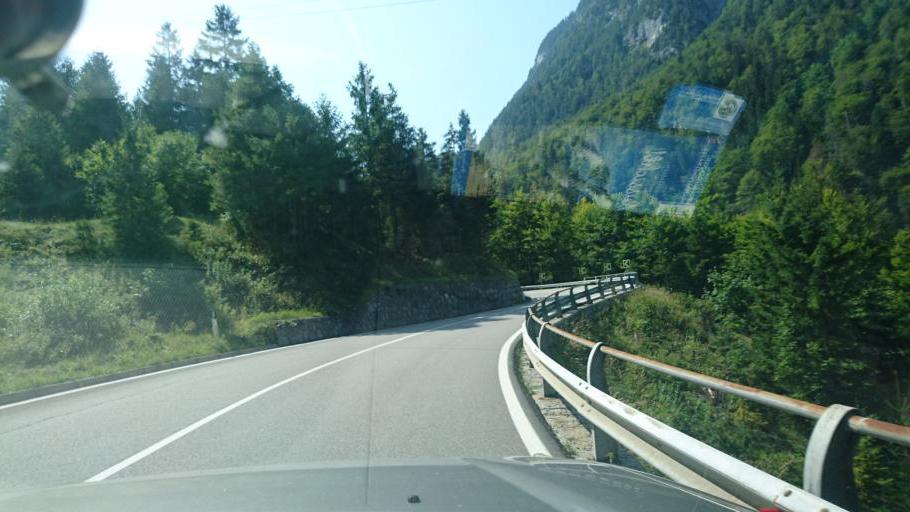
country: IT
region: Friuli Venezia Giulia
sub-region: Provincia di Udine
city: Tarvisio
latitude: 46.4659
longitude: 13.5722
